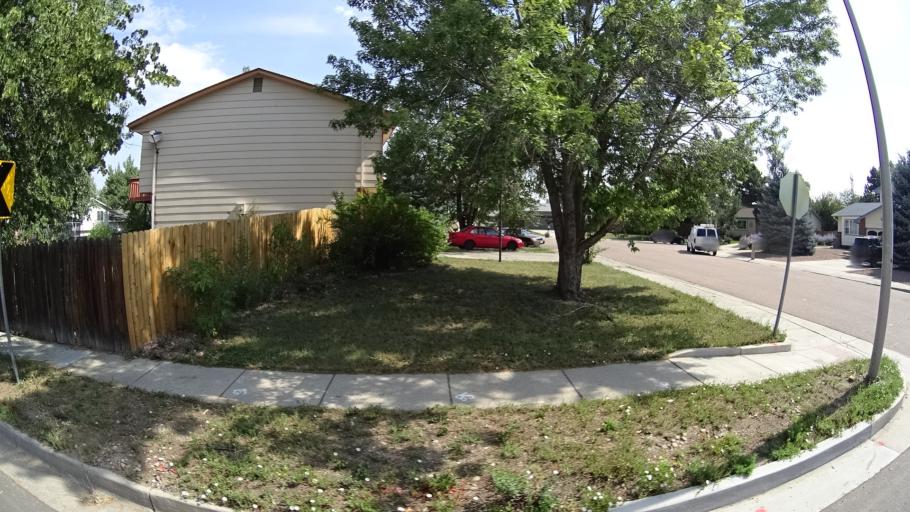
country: US
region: Colorado
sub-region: El Paso County
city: Colorado Springs
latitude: 38.9269
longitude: -104.7868
